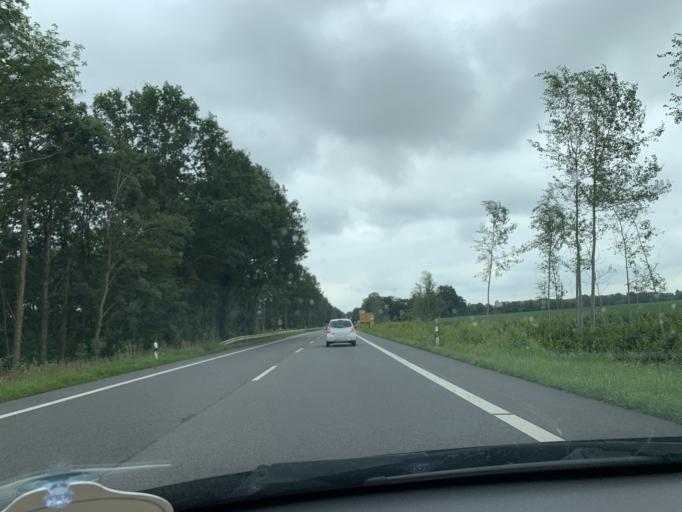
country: DE
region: North Rhine-Westphalia
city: Lengerich
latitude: 52.1752
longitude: 7.8480
